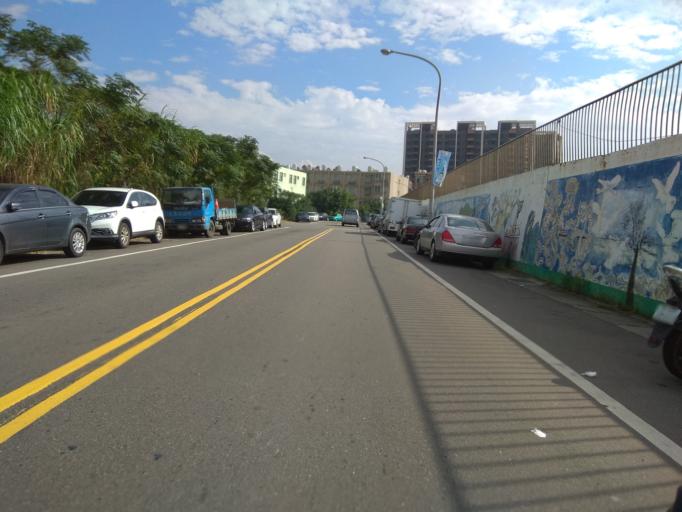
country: TW
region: Taiwan
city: Taoyuan City
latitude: 25.0642
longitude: 121.1924
